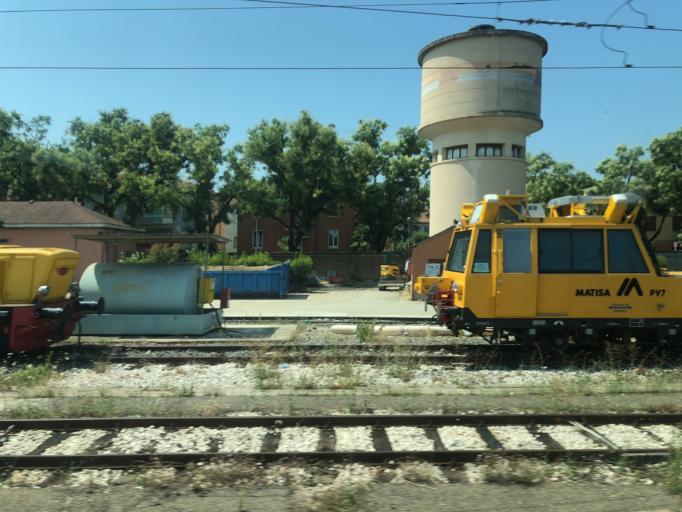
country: IT
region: Emilia-Romagna
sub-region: Provincia di Ravenna
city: Faenza
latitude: 44.2924
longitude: 11.8860
